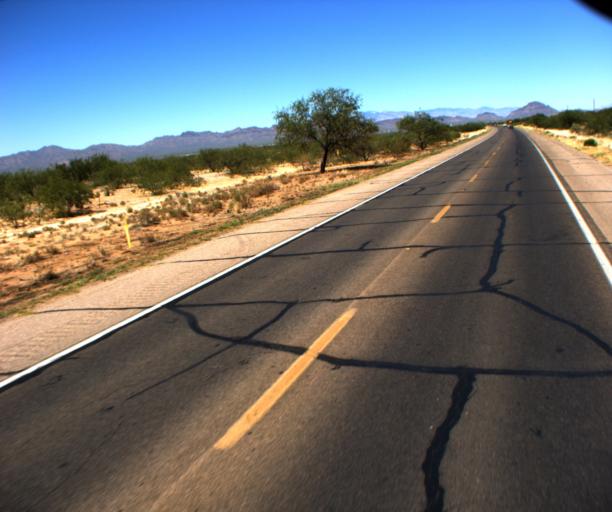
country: US
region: Arizona
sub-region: Pima County
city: Valencia West
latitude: 32.1179
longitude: -111.2104
